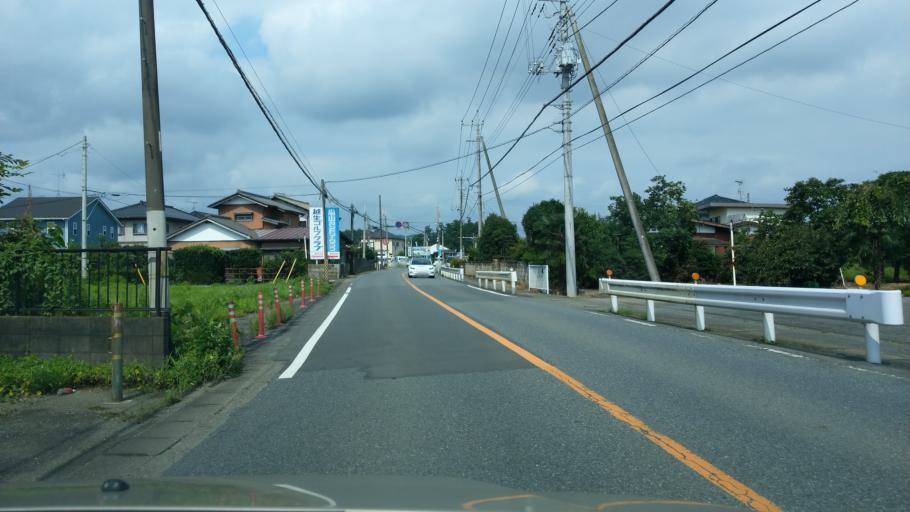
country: JP
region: Saitama
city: Ogawa
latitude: 36.0342
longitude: 139.3447
